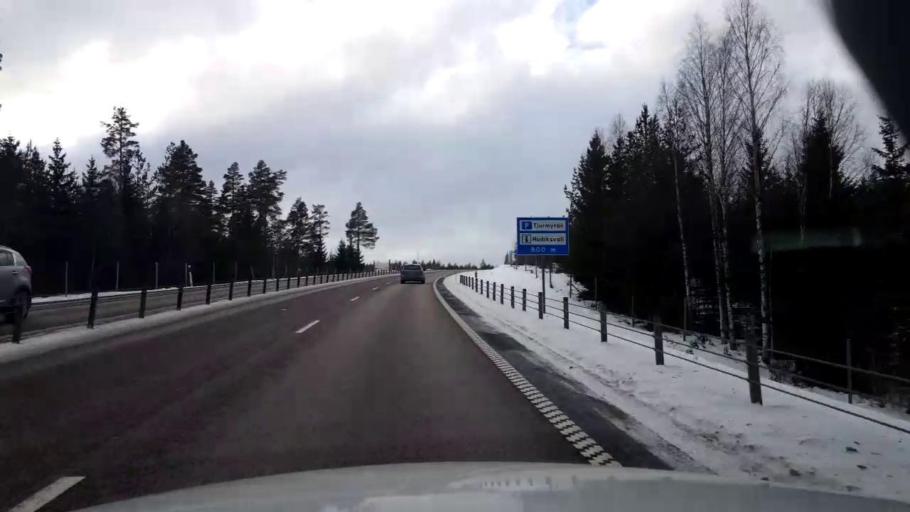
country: SE
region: Gaevleborg
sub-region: Hudiksvalls Kommun
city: Hudiksvall
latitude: 61.7949
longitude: 17.1655
